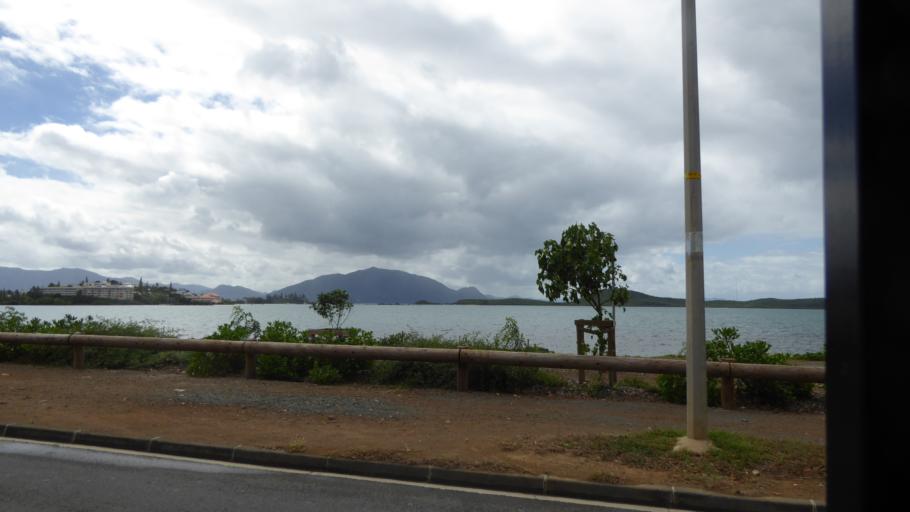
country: NC
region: South Province
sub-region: Noumea
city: Noumea
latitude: -22.2884
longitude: 166.4582
